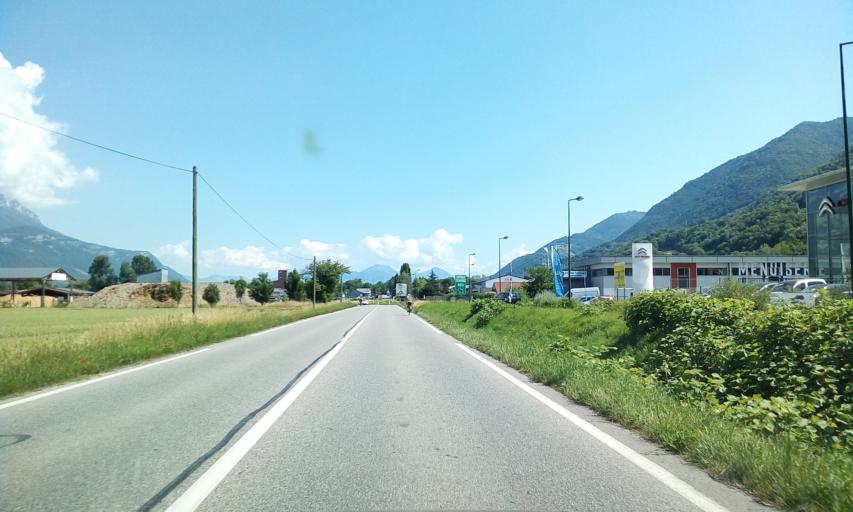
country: FR
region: Rhone-Alpes
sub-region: Departement de l'Isere
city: Tencin
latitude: 45.3255
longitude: 5.9685
